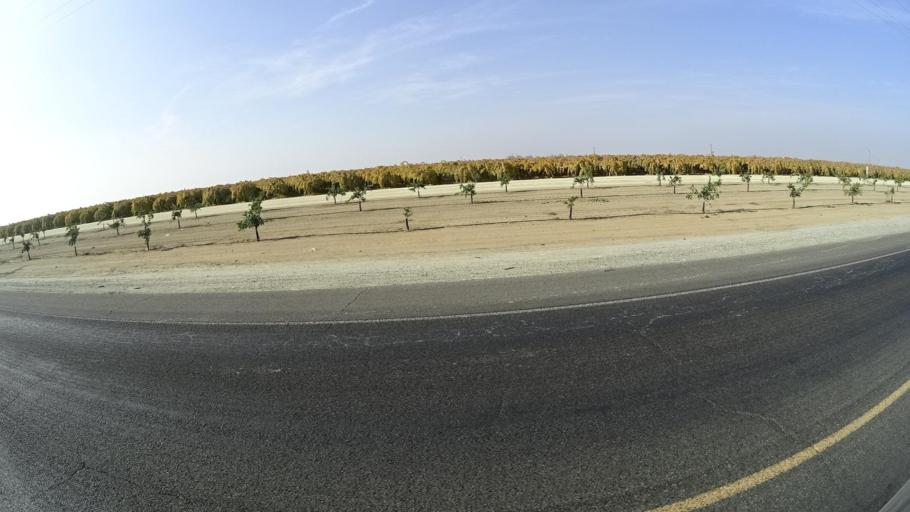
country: US
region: California
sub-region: Tulare County
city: Richgrove
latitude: 35.7298
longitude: -119.1523
